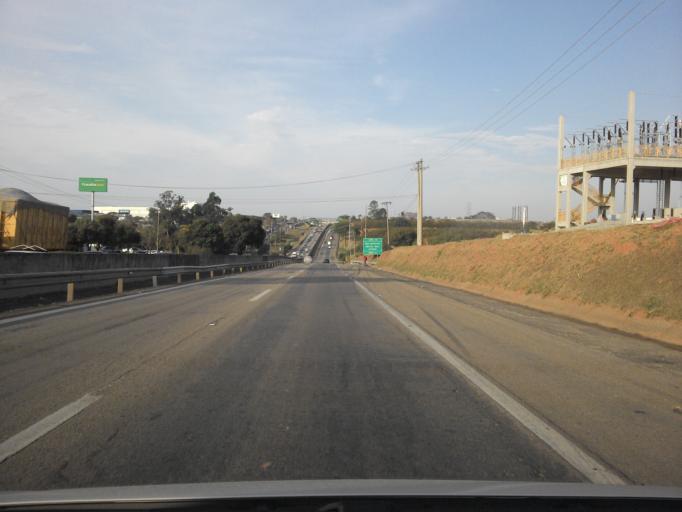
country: BR
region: Sao Paulo
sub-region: Hortolandia
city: Hortolandia
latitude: -22.8994
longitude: -47.1958
